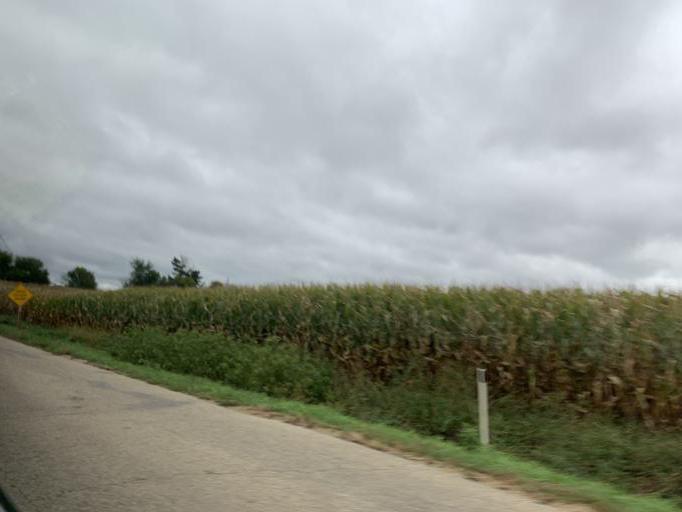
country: US
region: Wisconsin
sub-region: Sauk County
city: Prairie du Sac
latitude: 43.2839
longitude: -89.7789
